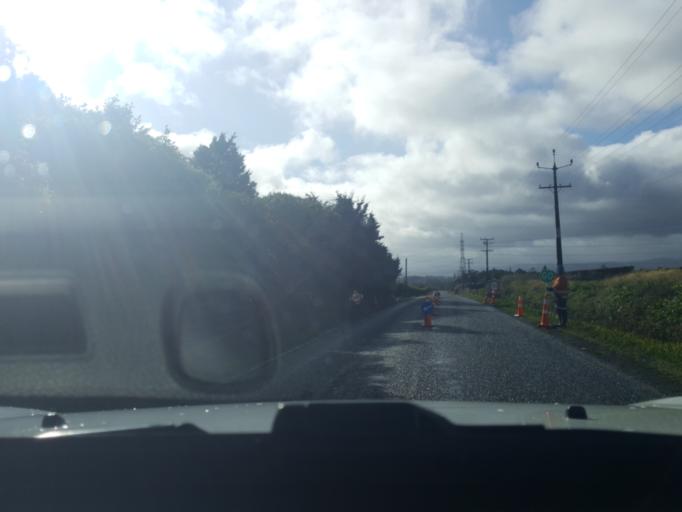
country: NZ
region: Auckland
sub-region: Auckland
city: Pukekohe East
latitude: -37.3092
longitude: 174.9907
